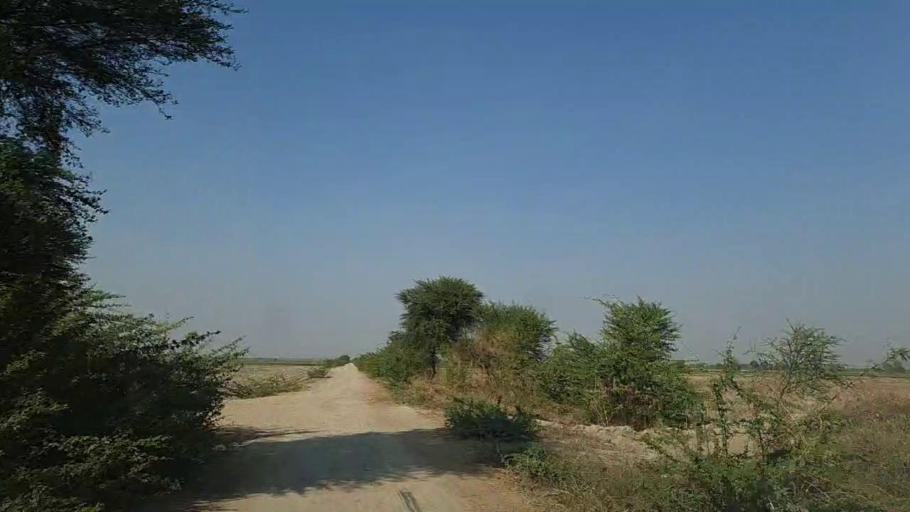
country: PK
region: Sindh
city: Naukot
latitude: 24.9074
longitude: 69.4876
